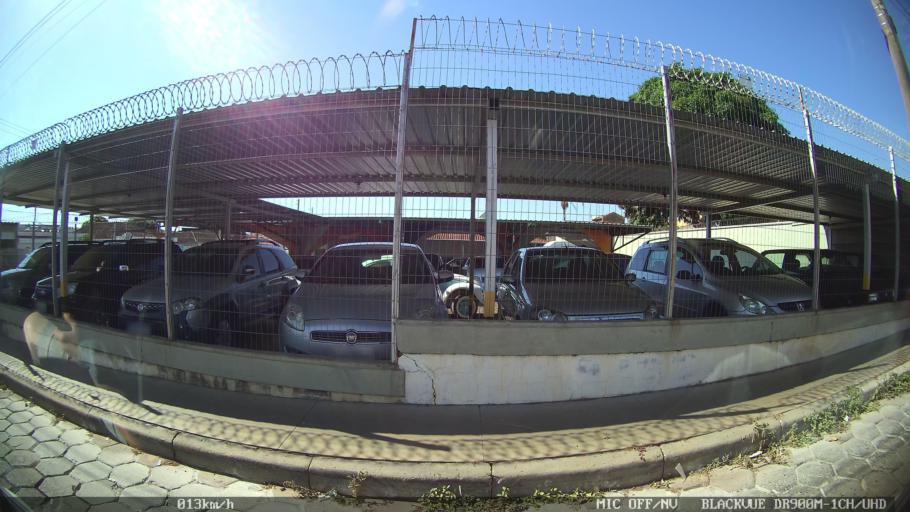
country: BR
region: Sao Paulo
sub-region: Batatais
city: Batatais
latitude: -20.8890
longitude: -47.5829
